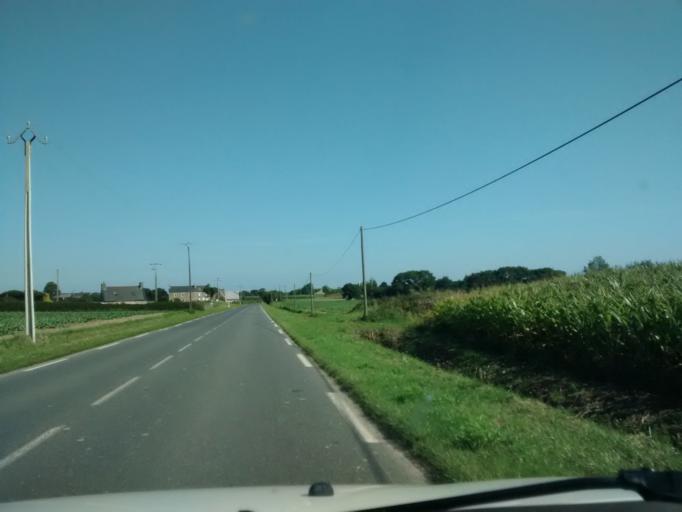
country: FR
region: Brittany
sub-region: Departement des Cotes-d'Armor
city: Tredarzec
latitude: 48.8213
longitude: -3.1885
